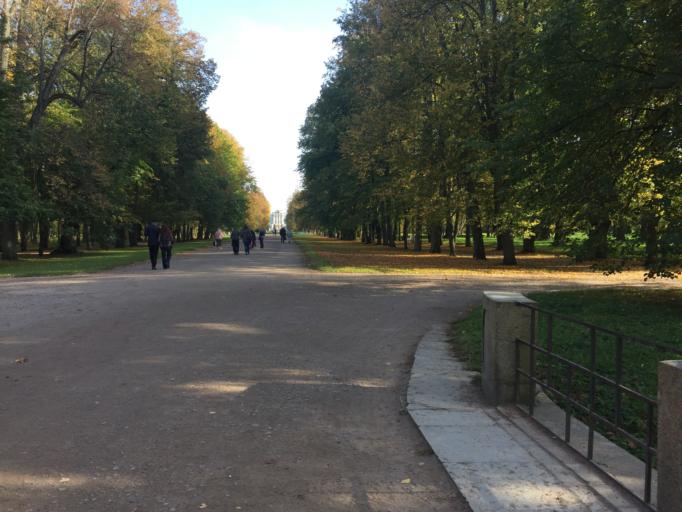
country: RU
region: St.-Petersburg
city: Pushkin
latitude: 59.7191
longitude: 30.3857
